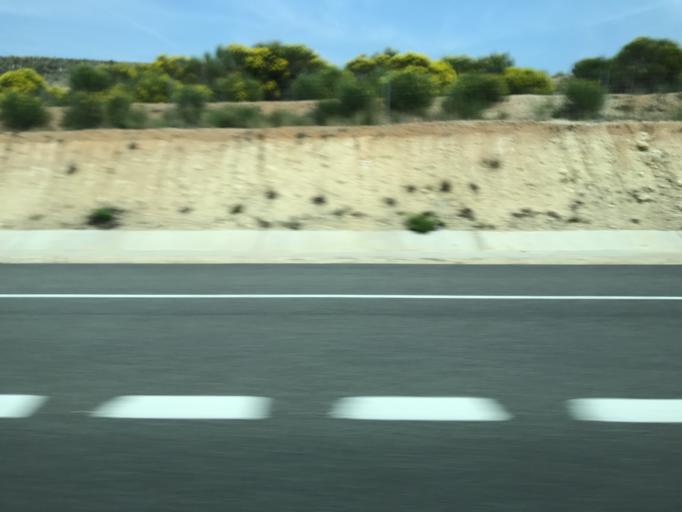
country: ES
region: Castille and Leon
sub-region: Provincia de Burgos
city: Bahabon de Esgueva
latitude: 41.8910
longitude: -3.7412
